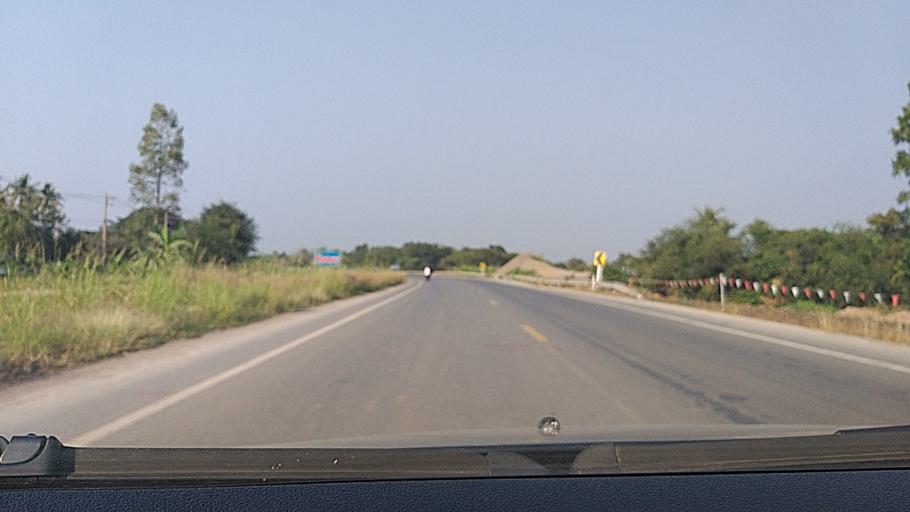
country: TH
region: Sing Buri
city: Phrom Buri
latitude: 14.8340
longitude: 100.4338
